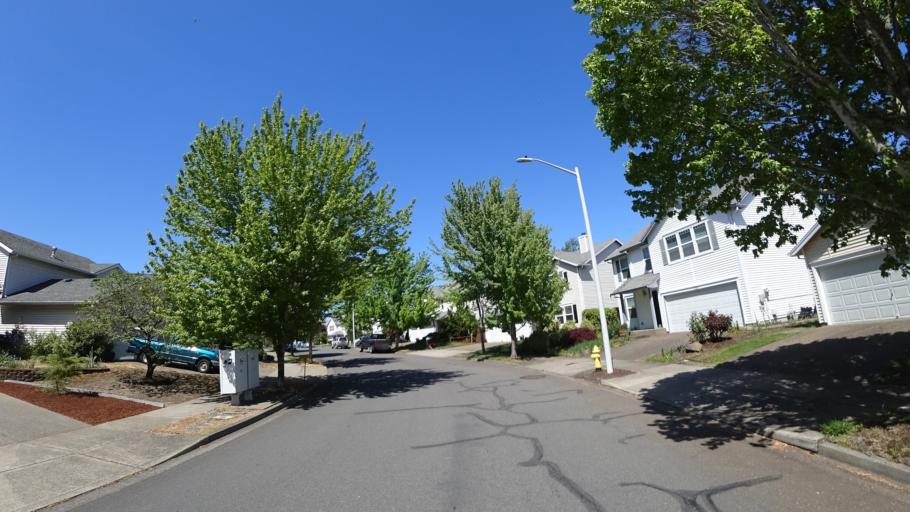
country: US
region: Oregon
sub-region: Washington County
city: Hillsboro
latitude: 45.5064
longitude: -122.9486
